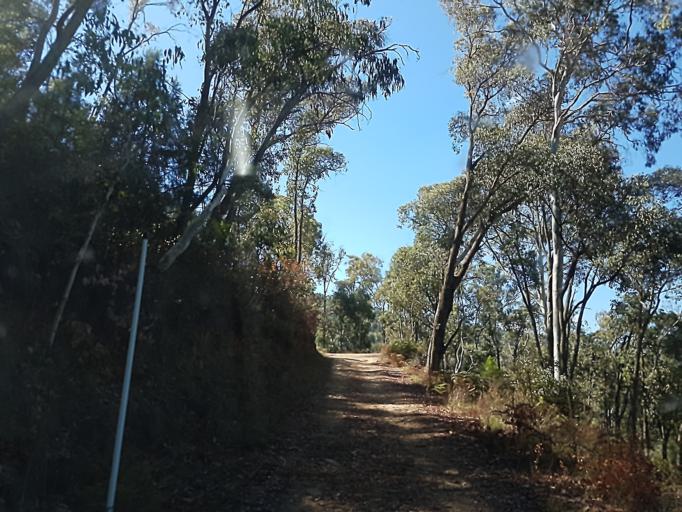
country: AU
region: Victoria
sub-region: Alpine
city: Mount Beauty
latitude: -36.8798
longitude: 147.0416
